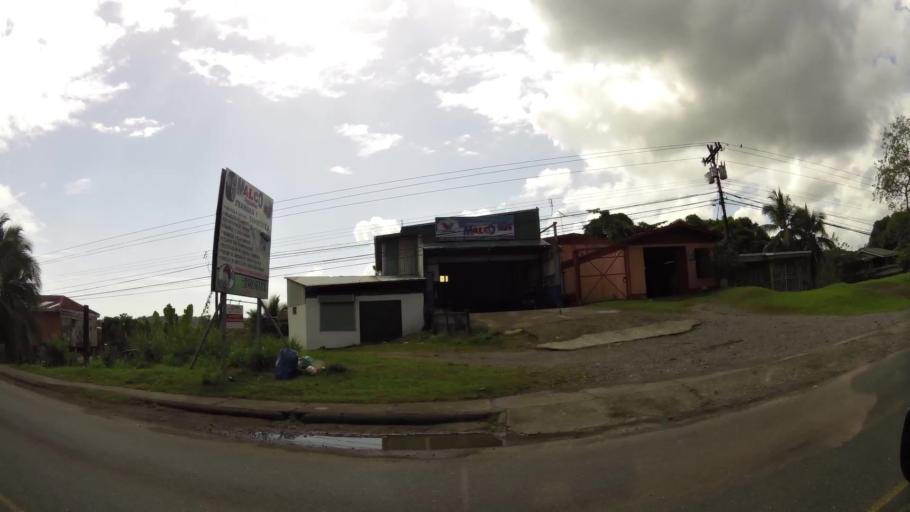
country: CR
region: Limon
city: Limon
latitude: 9.9853
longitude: -83.0514
